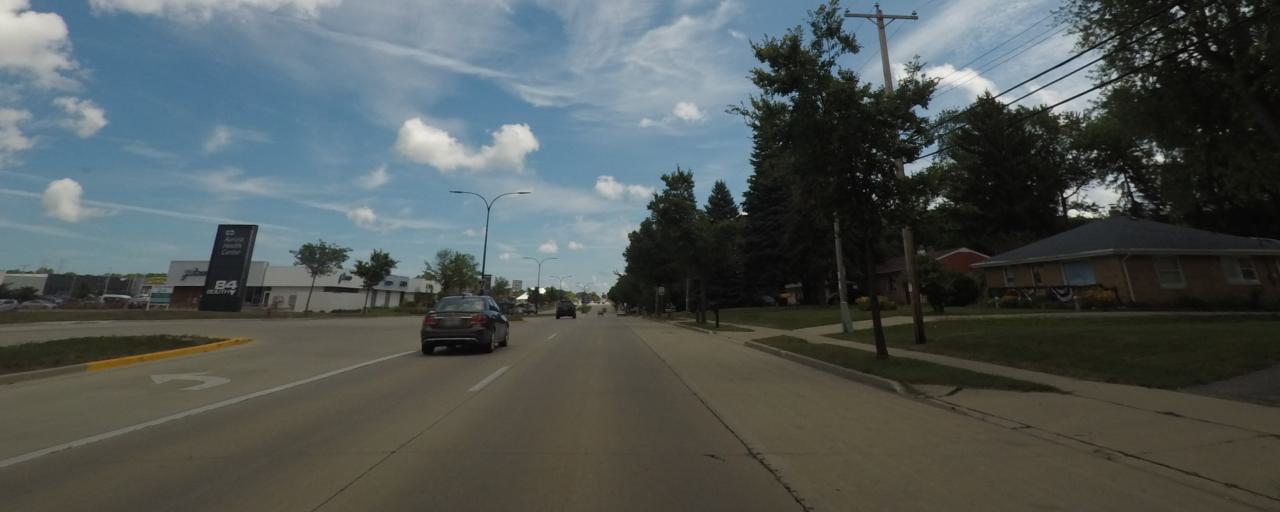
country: US
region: Wisconsin
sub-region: Milwaukee County
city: Greenfield
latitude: 42.9591
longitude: -88.0253
